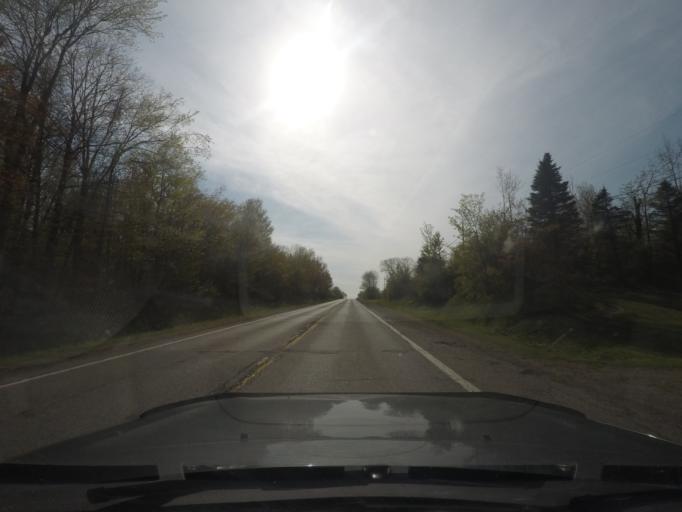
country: US
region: Michigan
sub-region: Berrien County
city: Buchanan
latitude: 41.7932
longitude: -86.4372
